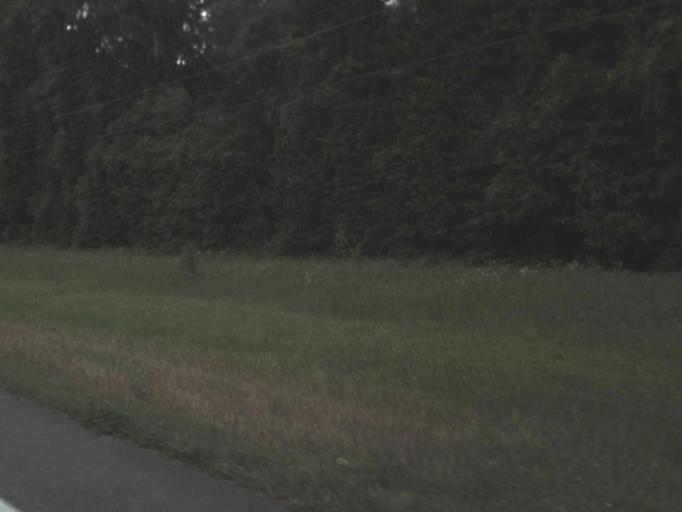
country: US
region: Florida
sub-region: Alachua County
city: Gainesville
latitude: 29.5676
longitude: -82.3934
